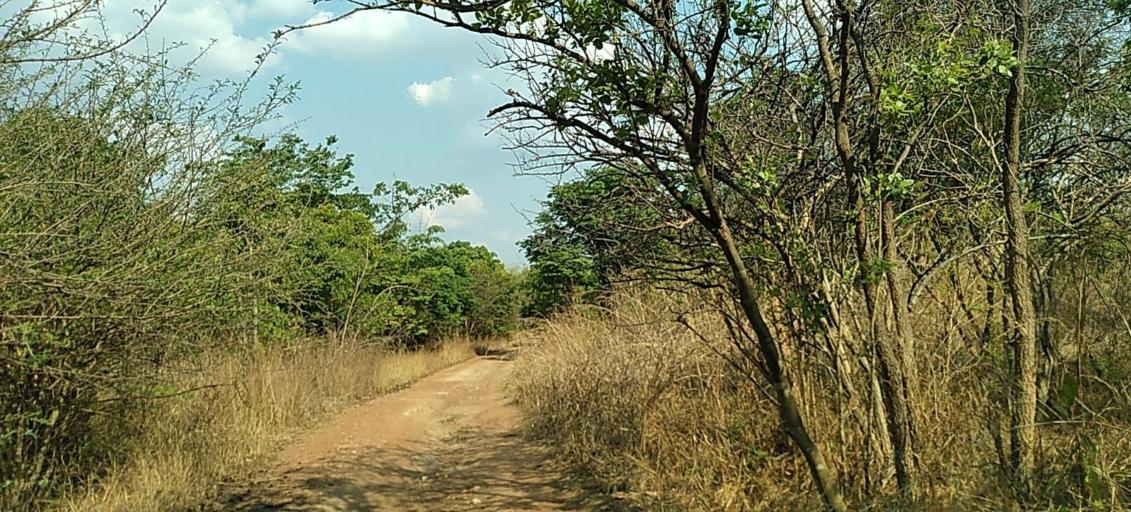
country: ZM
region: Copperbelt
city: Luanshya
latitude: -13.1654
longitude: 28.3458
